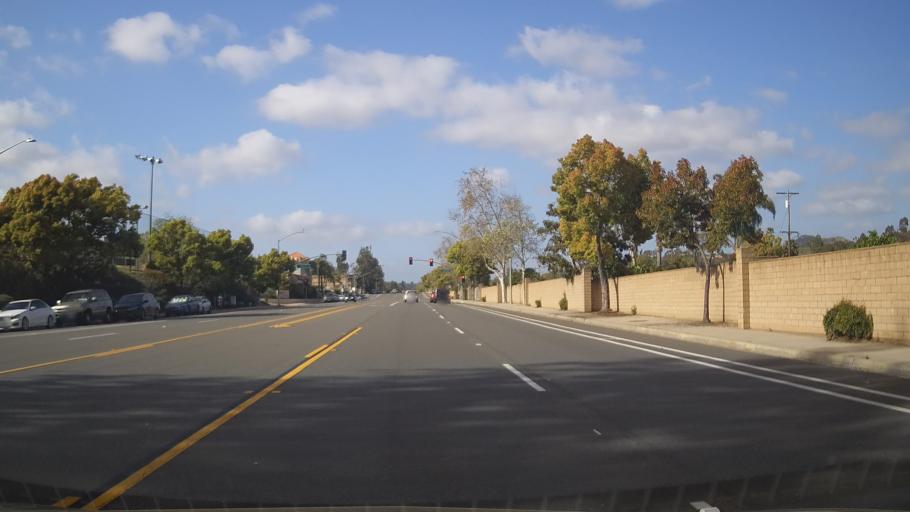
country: US
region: California
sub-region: San Diego County
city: Poway
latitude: 32.9577
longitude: -117.0624
